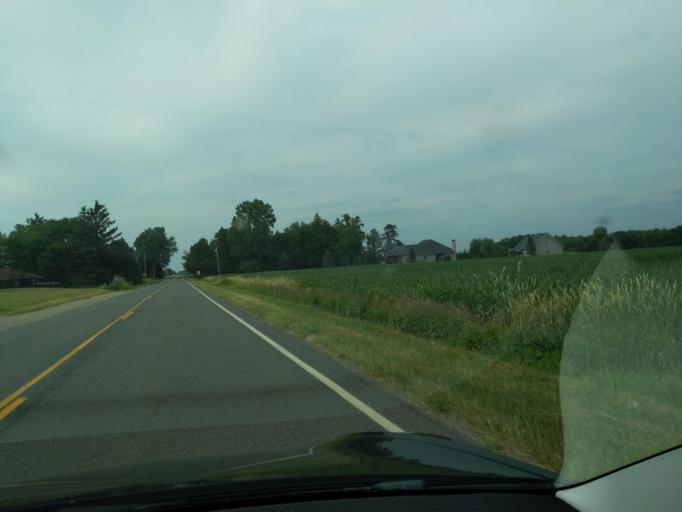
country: US
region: Michigan
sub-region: Clinton County
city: DeWitt
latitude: 42.9041
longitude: -84.6022
